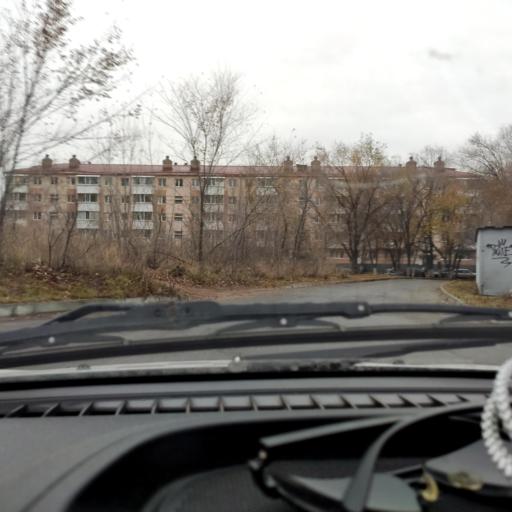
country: RU
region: Samara
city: Zhigulevsk
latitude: 53.4656
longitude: 49.5403
